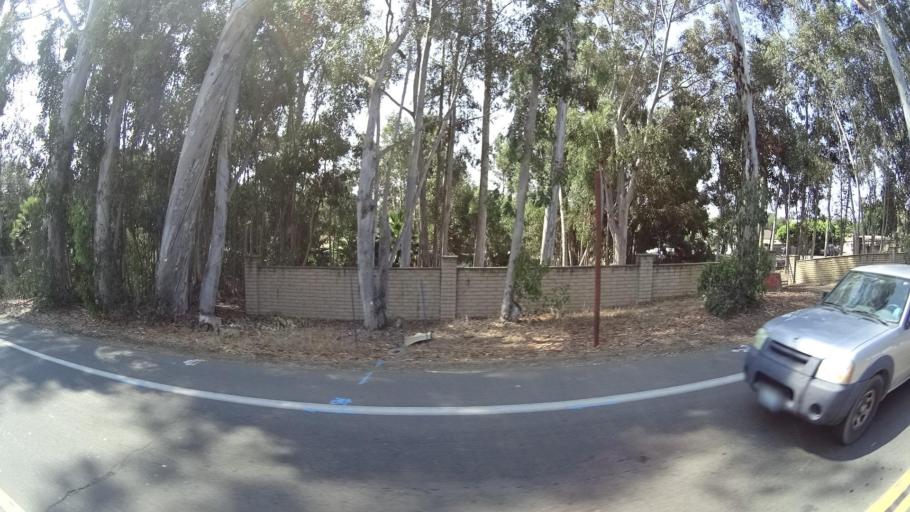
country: US
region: California
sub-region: San Diego County
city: Fallbrook
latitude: 33.3875
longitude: -117.2339
